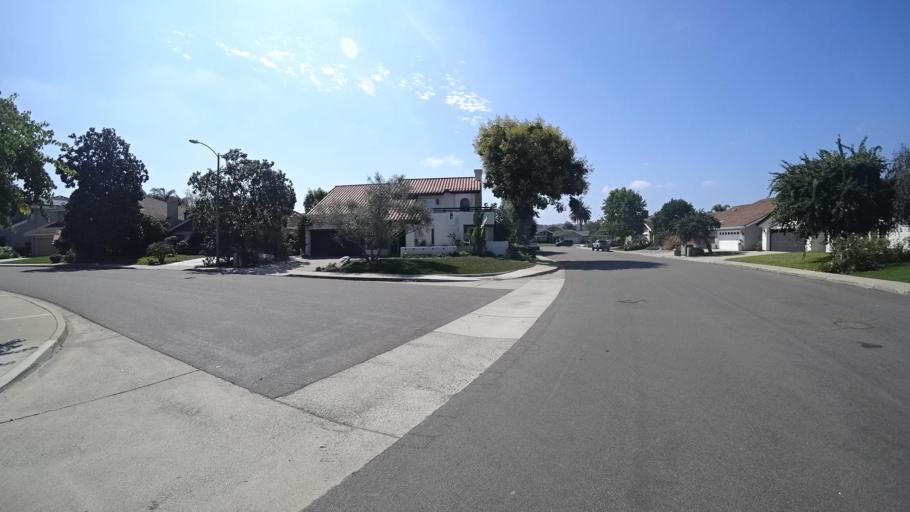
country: US
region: California
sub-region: San Diego County
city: Fairbanks Ranch
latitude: 32.9882
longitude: -117.2137
